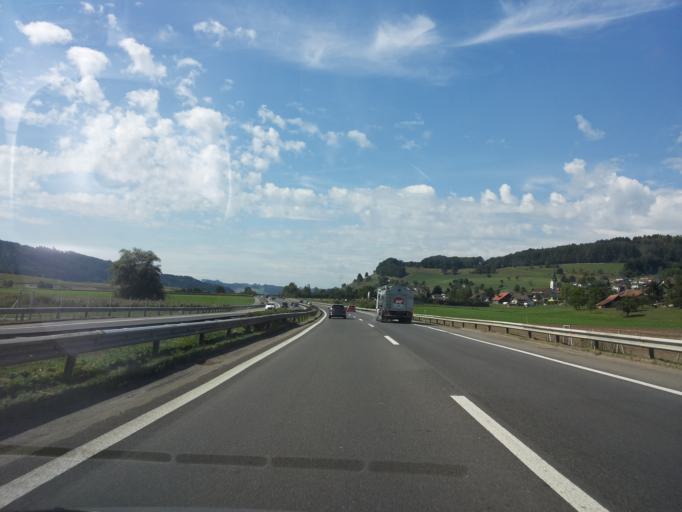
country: CH
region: Lucerne
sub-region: Willisau District
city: Wauwil
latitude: 47.2080
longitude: 8.0275
